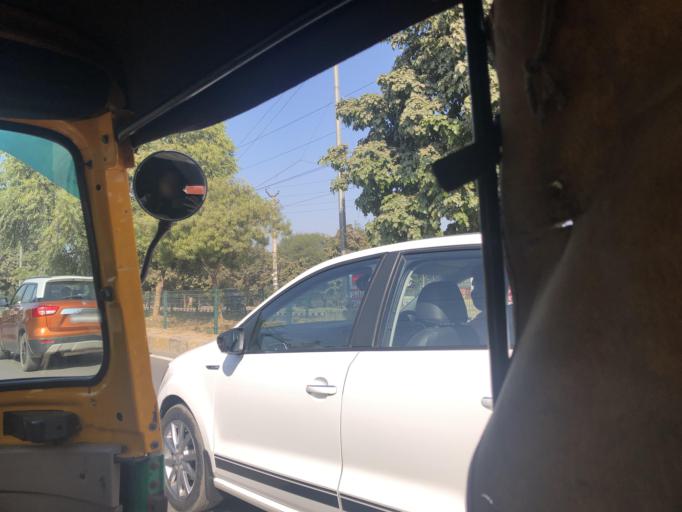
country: IN
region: Haryana
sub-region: Gurgaon
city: Gurgaon
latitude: 28.4402
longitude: 77.0876
